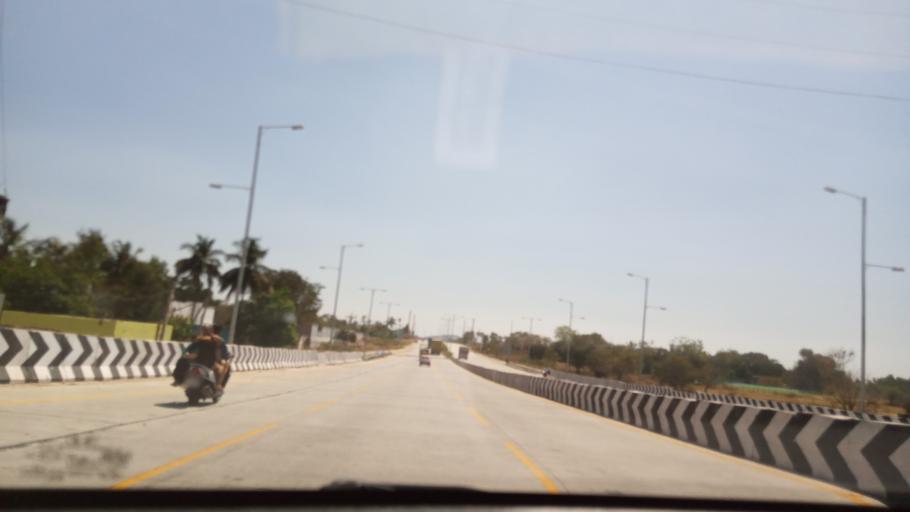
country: IN
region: Andhra Pradesh
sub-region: Chittoor
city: Palmaner
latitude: 13.1926
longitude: 78.5832
